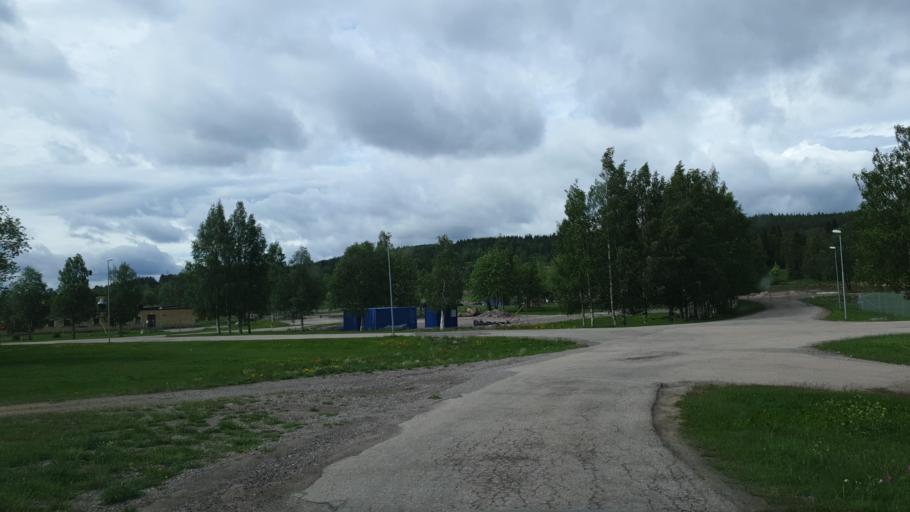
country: SE
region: Norrbotten
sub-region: Gallivare Kommun
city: Malmberget
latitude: 67.1774
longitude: 20.6676
